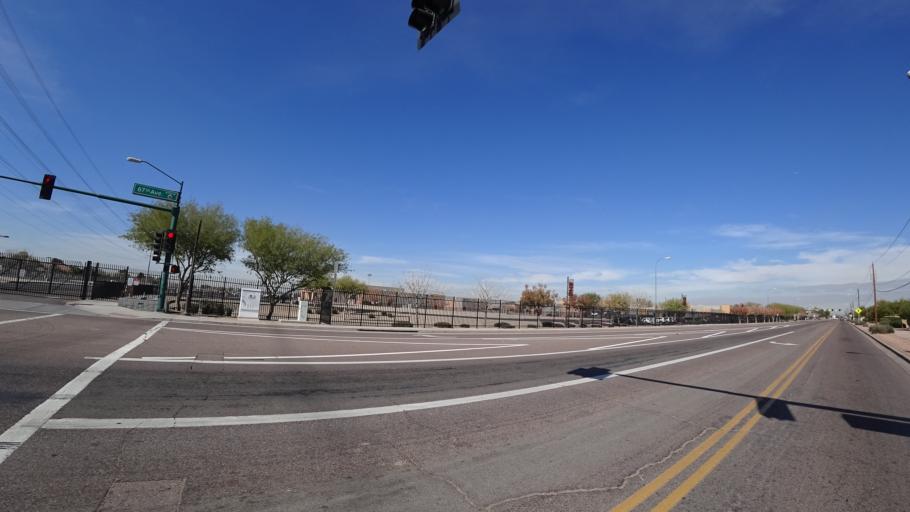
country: US
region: Arizona
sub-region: Maricopa County
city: Laveen
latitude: 33.4161
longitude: -112.2040
